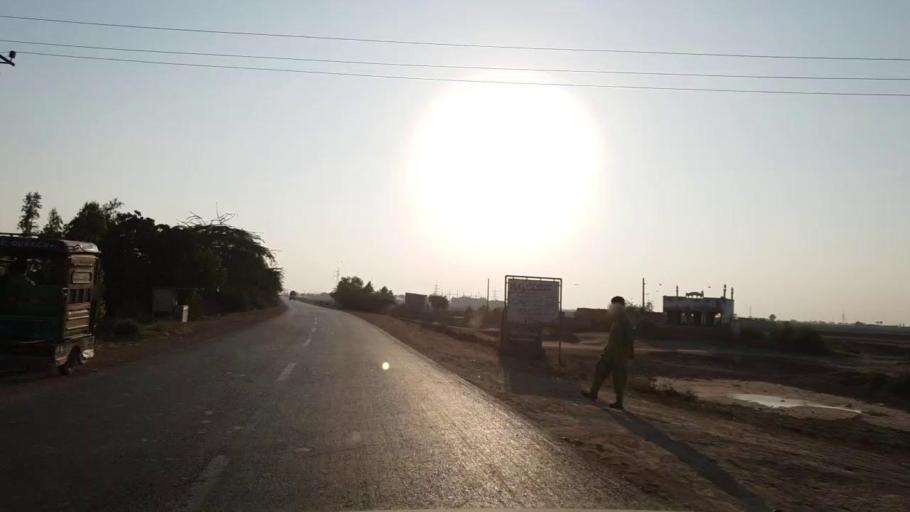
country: PK
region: Sindh
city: Daro Mehar
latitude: 24.6325
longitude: 68.1059
